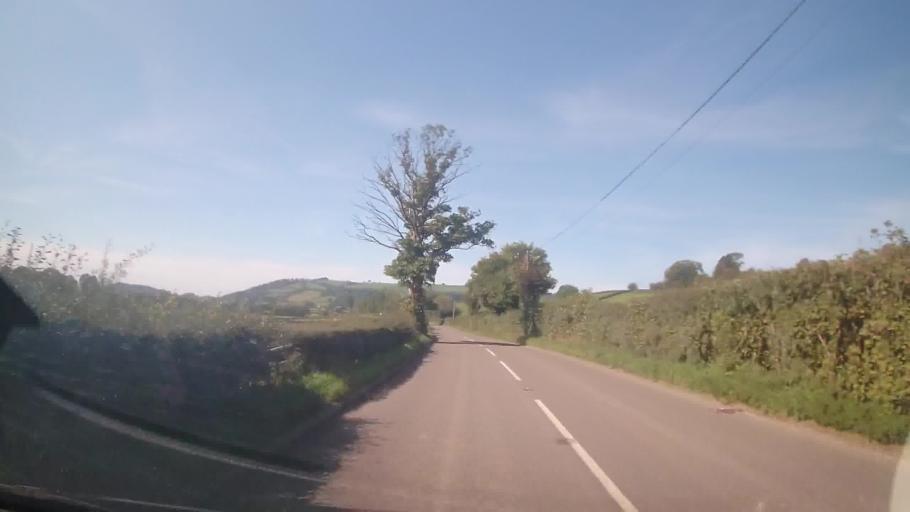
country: GB
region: Wales
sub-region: Sir Powys
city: Montgomery
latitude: 52.5293
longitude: -3.1243
